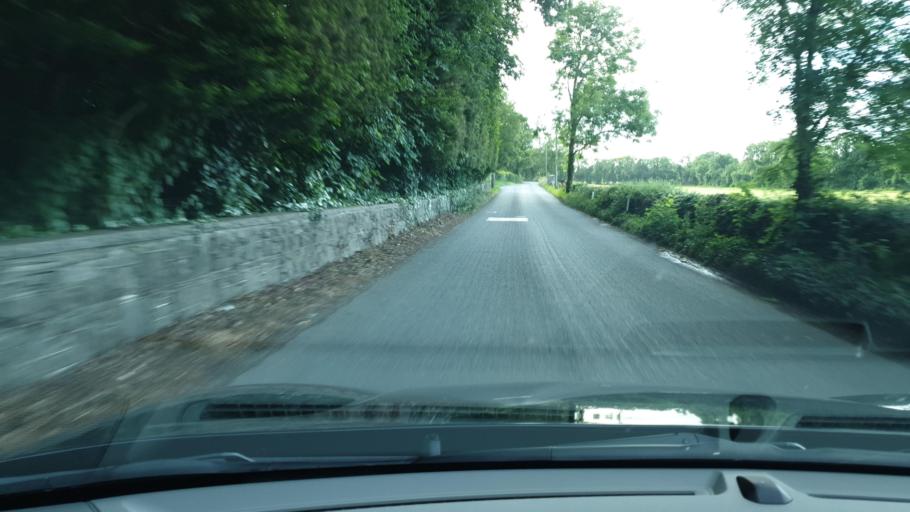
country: IE
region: Leinster
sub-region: An Mhi
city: Ratoath
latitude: 53.5374
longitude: -6.4342
